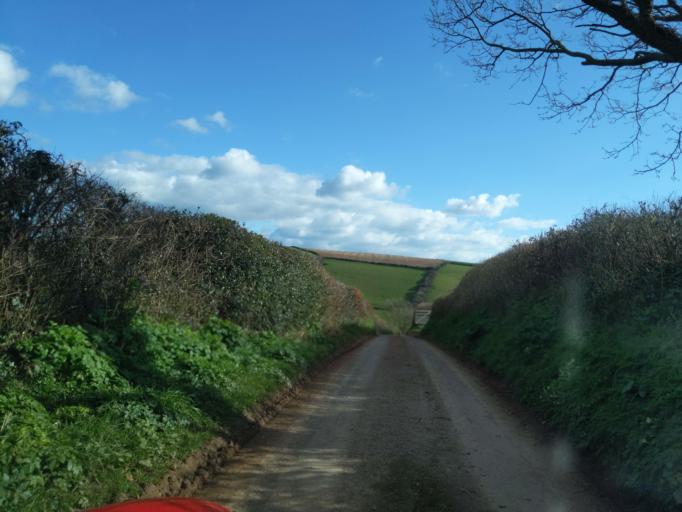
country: GB
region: England
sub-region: Devon
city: Kingsbridge
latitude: 50.2898
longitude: -3.7553
